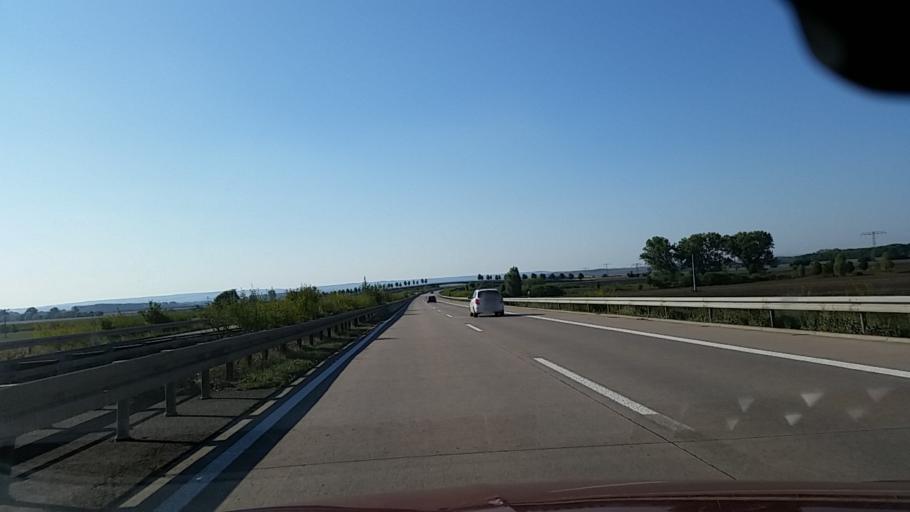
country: DE
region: Thuringia
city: Schlossvippach
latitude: 51.0860
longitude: 11.1255
